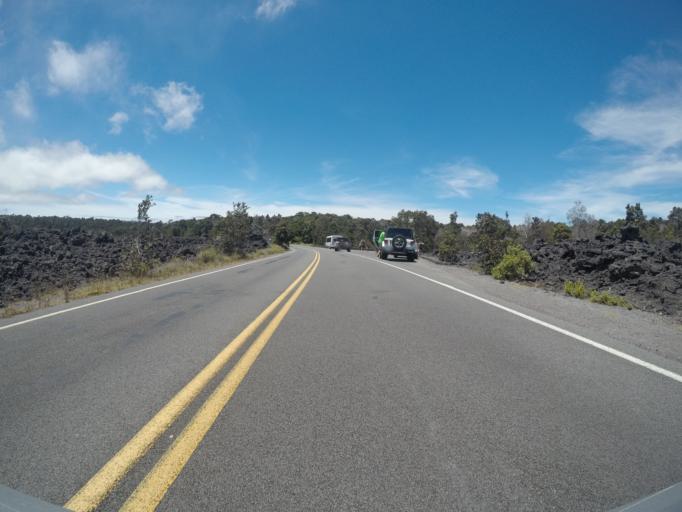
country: US
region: Hawaii
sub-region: Hawaii County
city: Volcano
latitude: 19.3995
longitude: -155.2534
